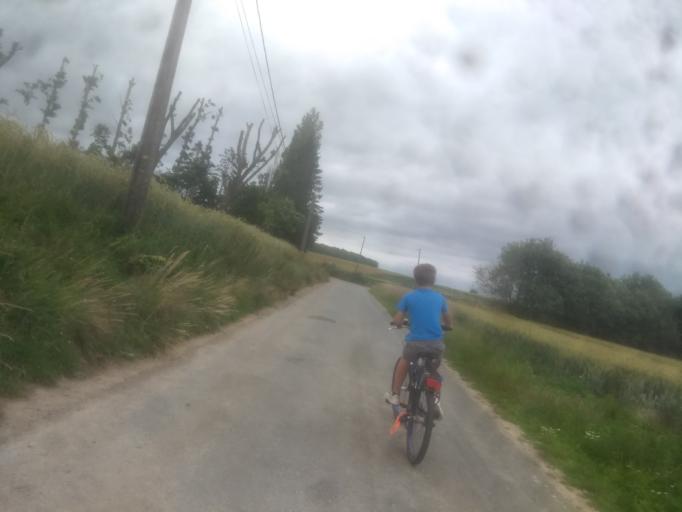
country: FR
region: Nord-Pas-de-Calais
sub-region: Departement du Pas-de-Calais
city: Mont-Saint-Eloi
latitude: 50.3559
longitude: 2.7061
